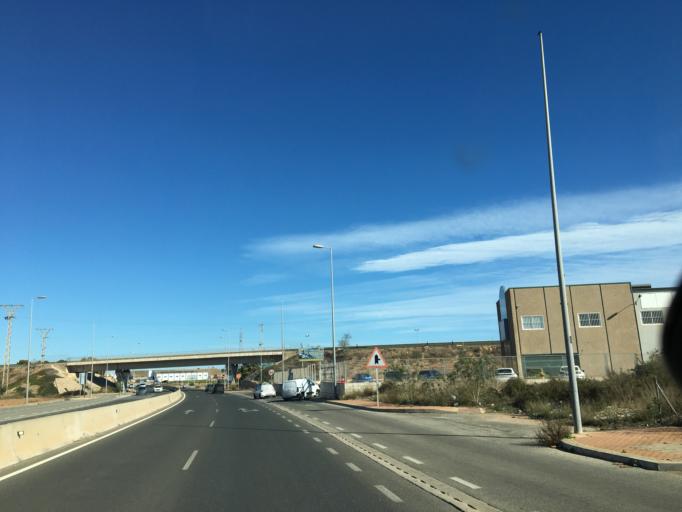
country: ES
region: Murcia
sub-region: Murcia
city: Cartagena
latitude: 37.6405
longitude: -0.9871
